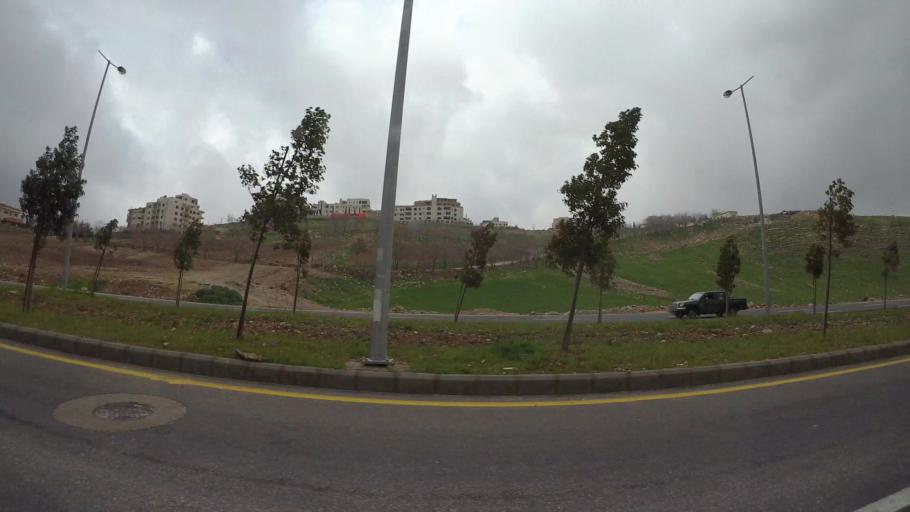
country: JO
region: Amman
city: Al Bunayyat ash Shamaliyah
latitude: 31.9336
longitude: 35.8953
